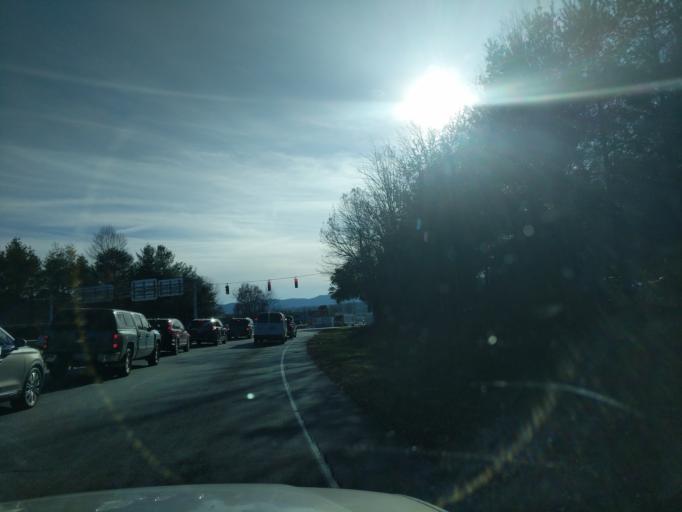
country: US
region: North Carolina
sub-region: Henderson County
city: Hendersonville
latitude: 35.3400
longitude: -82.4423
